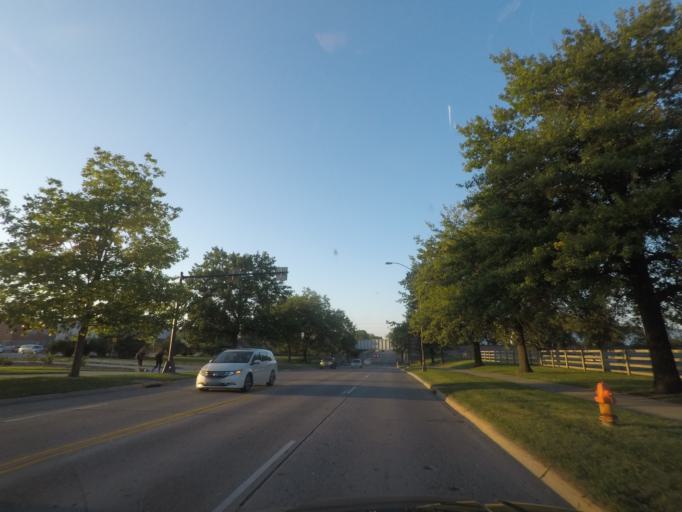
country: US
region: Iowa
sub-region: Story County
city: Ames
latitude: 42.0312
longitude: -93.6446
